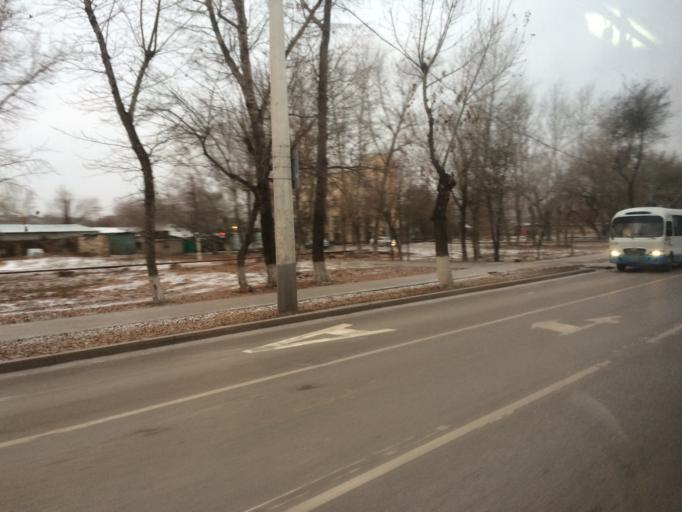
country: KZ
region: Astana Qalasy
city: Astana
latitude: 51.1650
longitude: 71.4558
